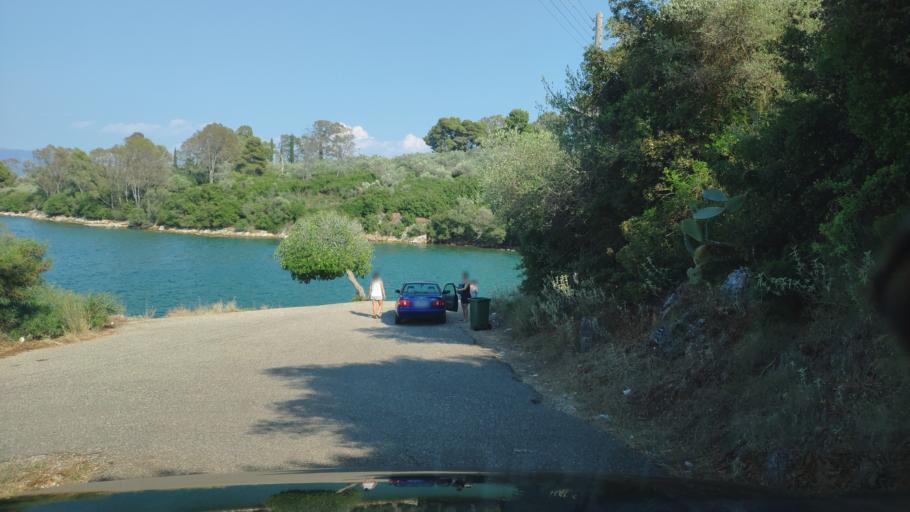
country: GR
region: West Greece
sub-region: Nomos Aitolias kai Akarnanias
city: Amfilochia
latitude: 38.9042
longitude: 21.1146
